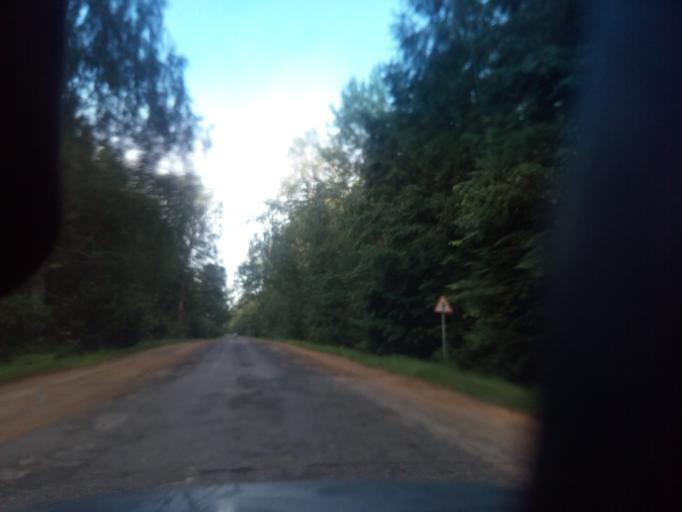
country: BY
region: Vitebsk
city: Dzisna
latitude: 55.6294
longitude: 28.2993
